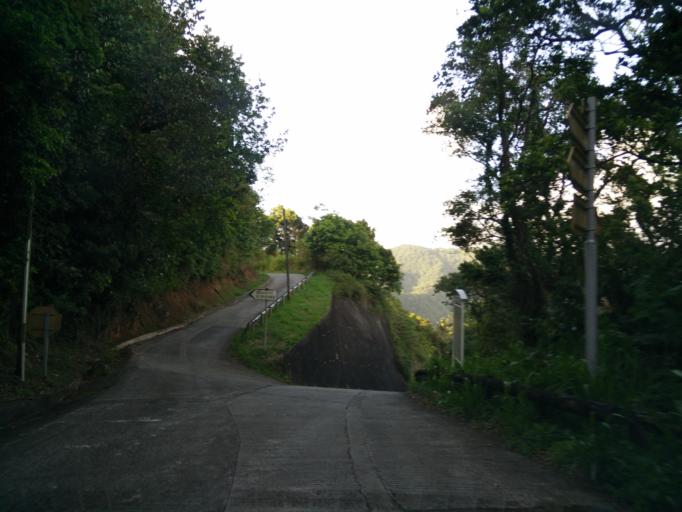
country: MQ
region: Martinique
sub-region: Martinique
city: Saint-Pierre
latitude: 14.7365
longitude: -61.1441
